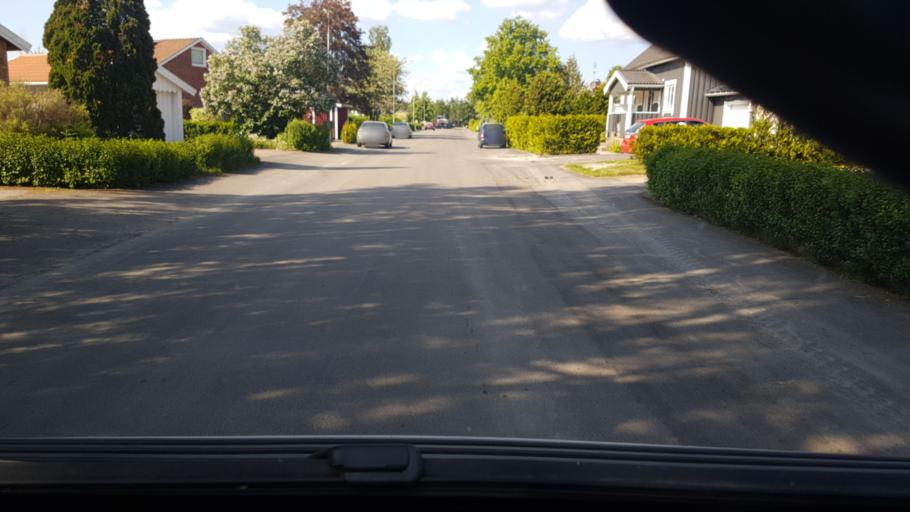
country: SE
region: Vaermland
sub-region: Eda Kommun
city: Charlottenberg
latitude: 59.8888
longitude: 12.3062
